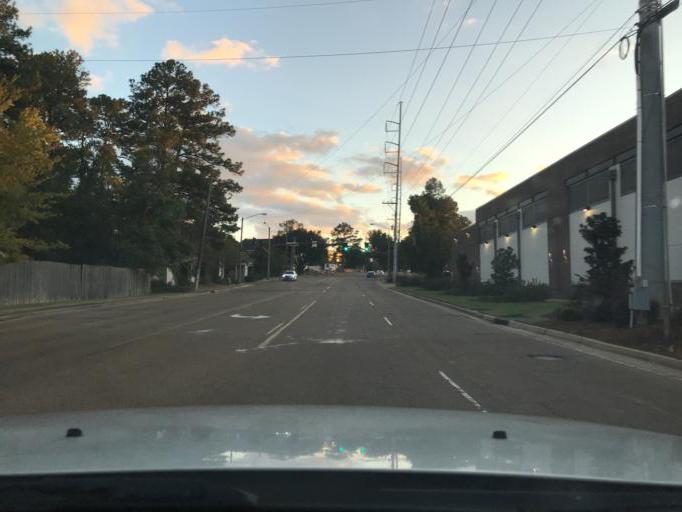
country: US
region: Mississippi
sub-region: Rankin County
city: Flowood
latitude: 32.3548
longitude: -90.1491
